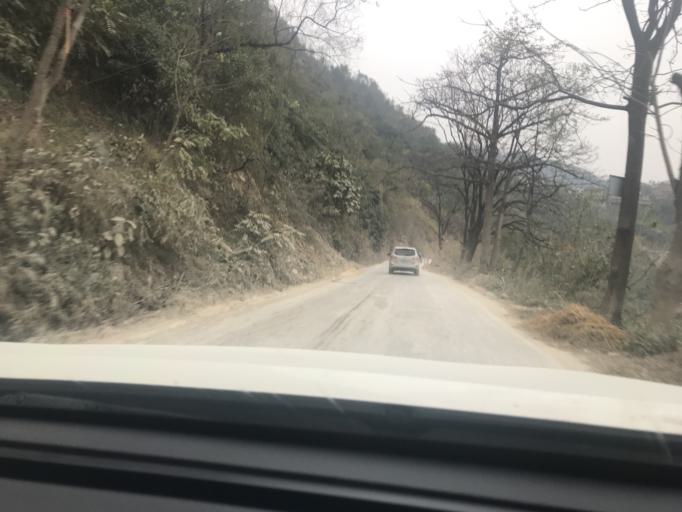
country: CN
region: Guangxi Zhuangzu Zizhiqu
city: Xinzhou
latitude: 24.9902
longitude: 105.8239
